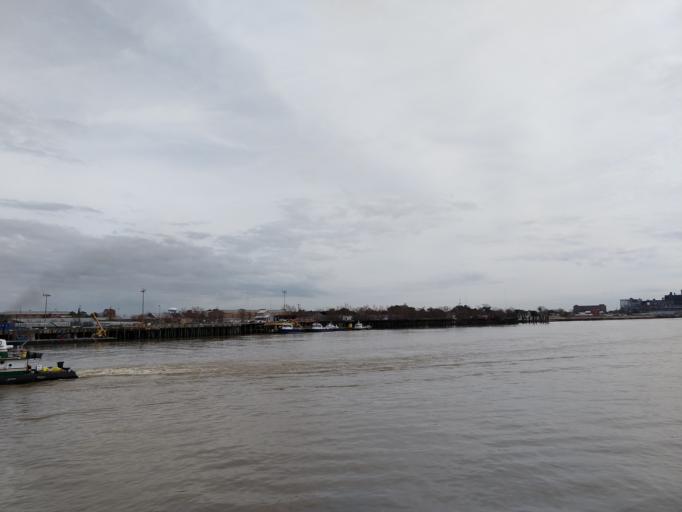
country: US
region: Louisiana
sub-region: Saint Bernard Parish
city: Arabi
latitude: 29.9502
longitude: -90.0174
